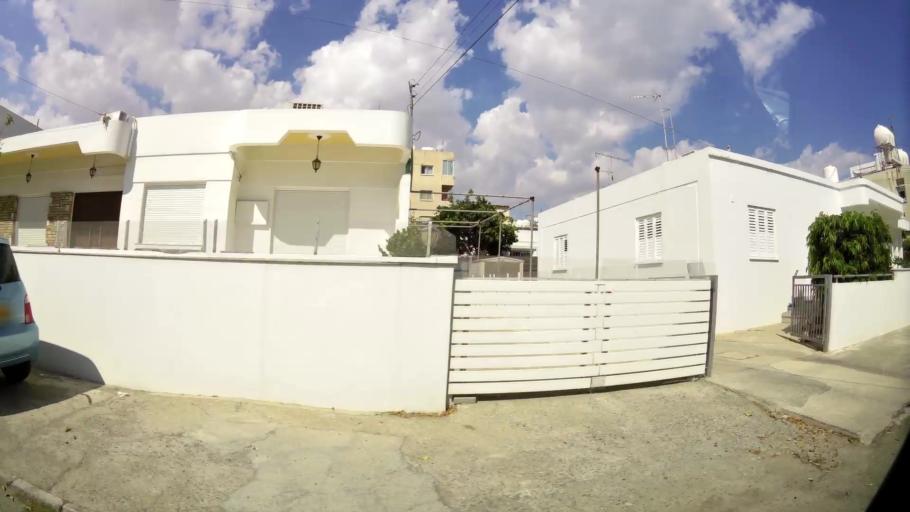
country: CY
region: Larnaka
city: Larnaca
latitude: 34.9174
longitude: 33.6161
